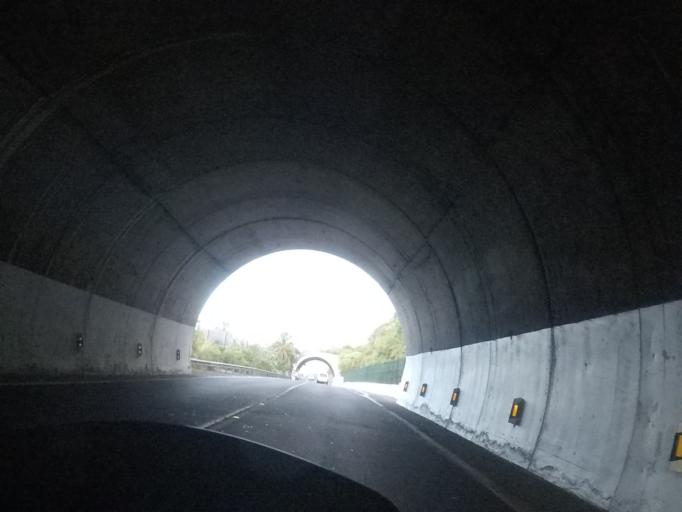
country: ES
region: Canary Islands
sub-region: Provincia de Santa Cruz de Tenerife
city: San Juan de la Rambla
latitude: 28.3931
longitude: -16.6476
